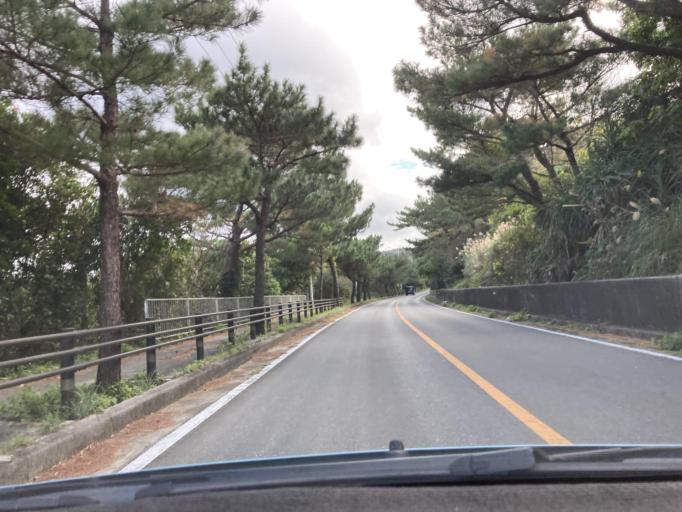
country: JP
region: Okinawa
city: Nago
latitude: 26.8627
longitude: 128.2600
